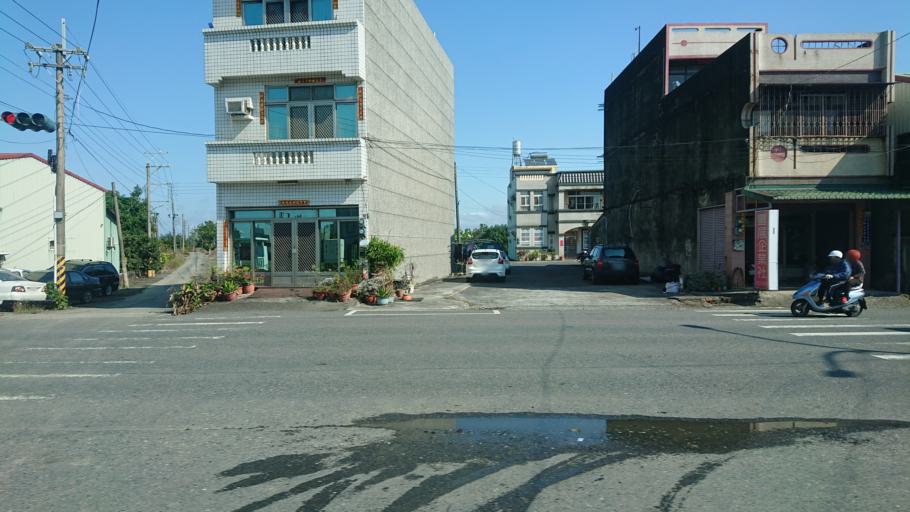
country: TW
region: Taiwan
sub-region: Chiayi
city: Taibao
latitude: 23.4391
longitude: 120.3842
